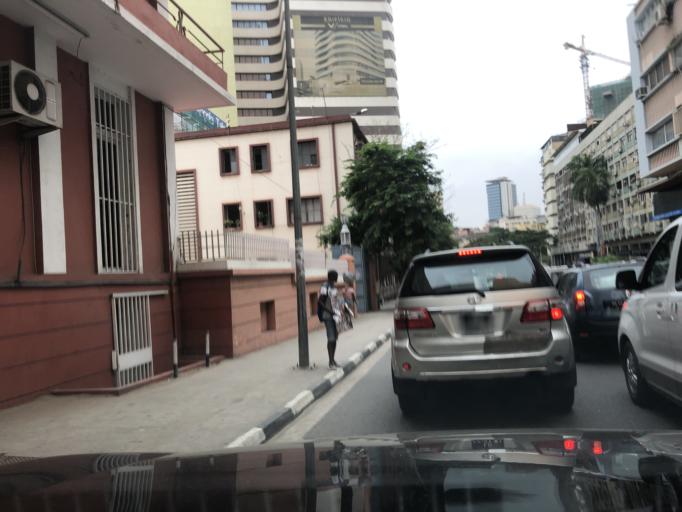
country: AO
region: Luanda
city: Luanda
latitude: -8.8175
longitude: 13.2298
